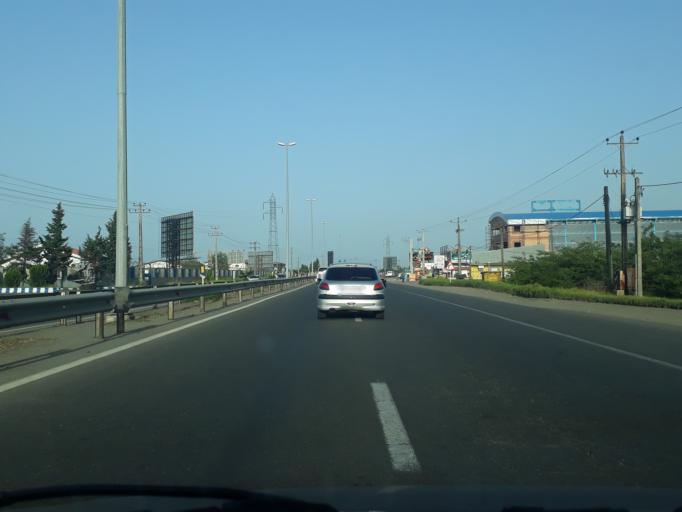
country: IR
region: Gilan
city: Bandar-e Anzali
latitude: 37.4600
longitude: 49.5859
